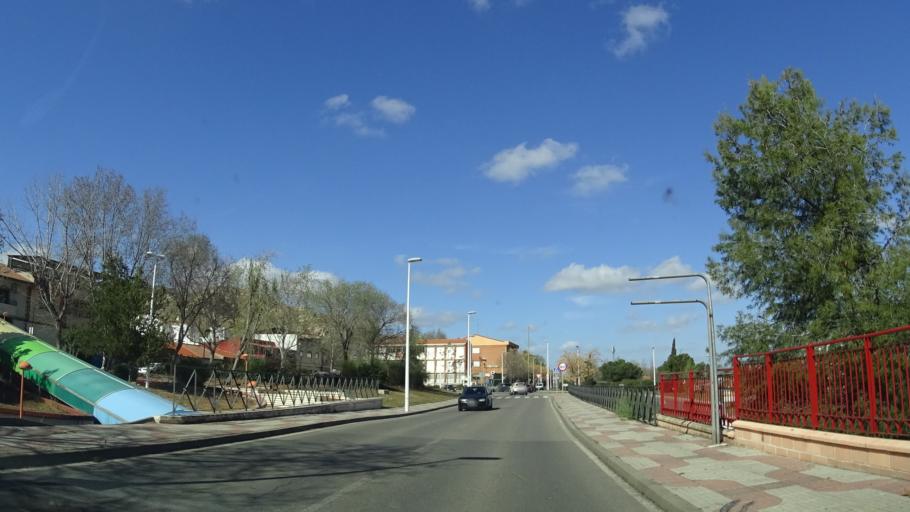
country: ES
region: Castille-La Mancha
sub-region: Provincia de Ciudad Real
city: Puertollano
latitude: 38.6897
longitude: -4.1133
